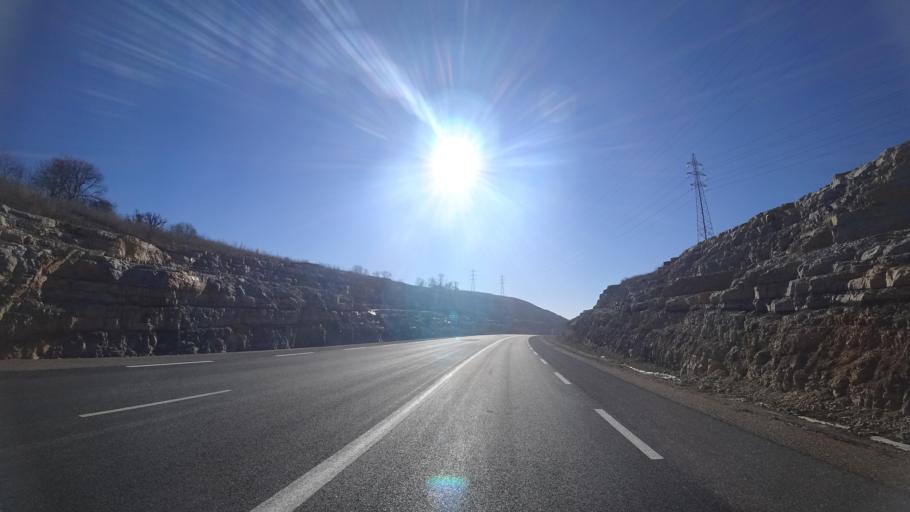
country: FR
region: Midi-Pyrenees
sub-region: Departement de l'Aveyron
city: Sebazac-Concoures
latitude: 44.3830
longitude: 2.6163
